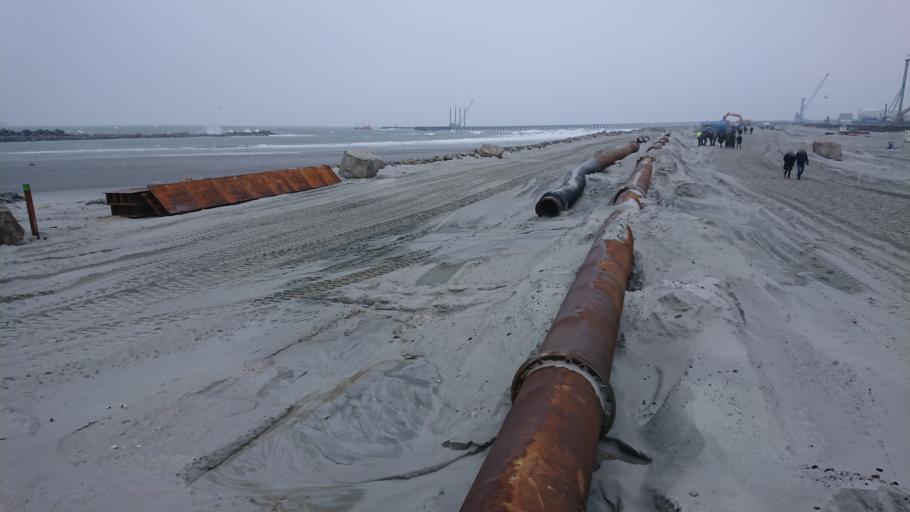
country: DK
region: North Denmark
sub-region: Frederikshavn Kommune
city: Skagen
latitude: 57.7195
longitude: 10.6048
